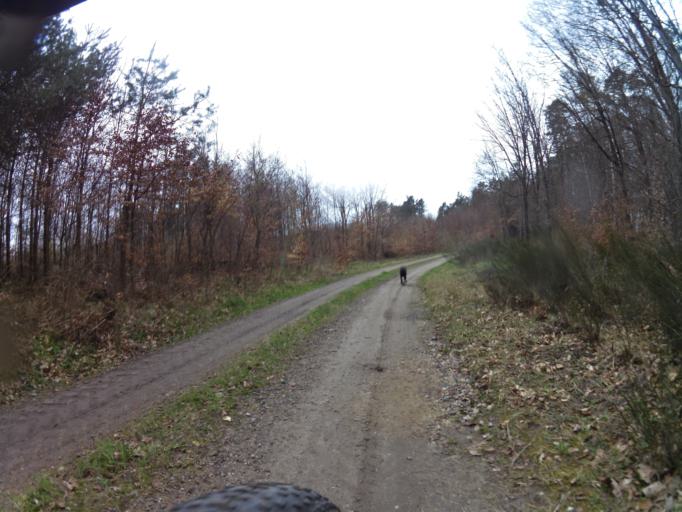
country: PL
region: West Pomeranian Voivodeship
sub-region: Powiat koszalinski
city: Polanow
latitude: 54.0716
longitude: 16.6221
